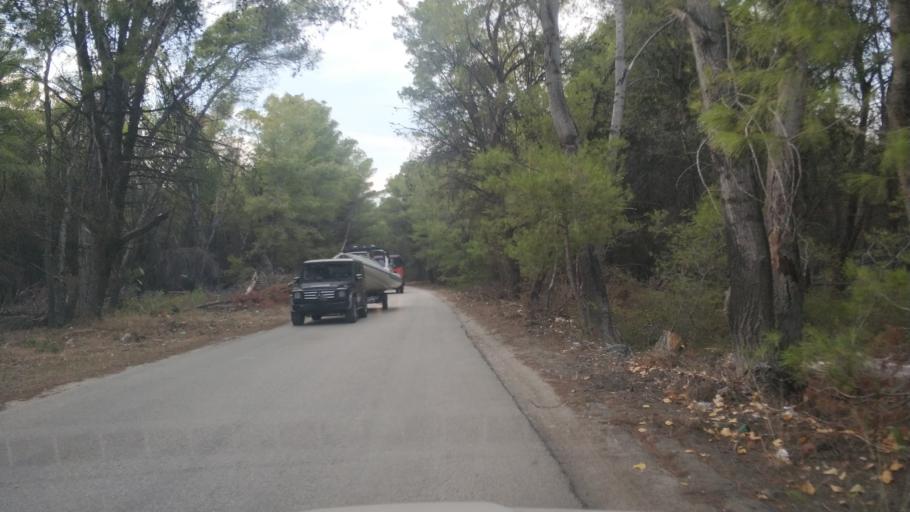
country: AL
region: Vlore
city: Vlore
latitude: 40.4855
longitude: 19.4455
